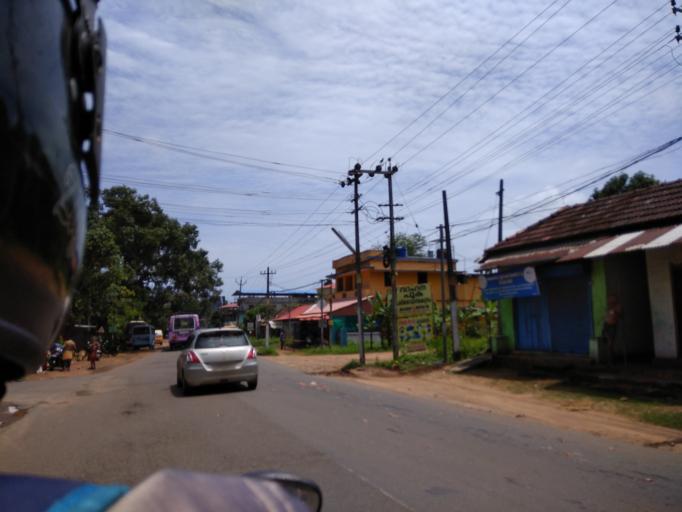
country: IN
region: Kerala
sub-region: Thrissur District
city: Trichur
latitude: 10.4975
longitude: 76.1481
